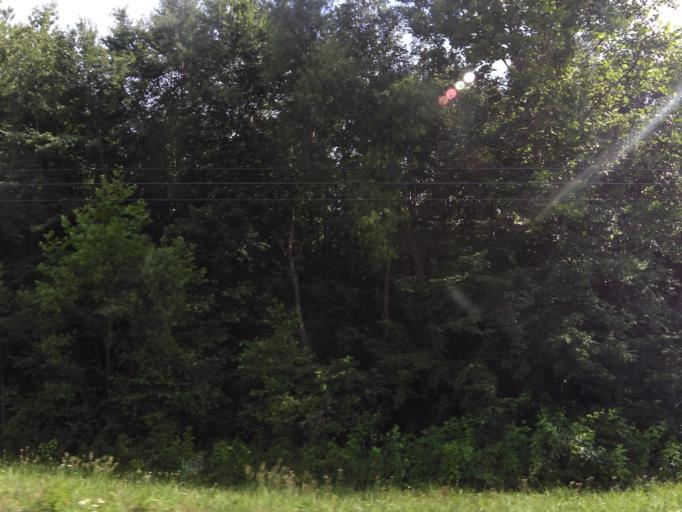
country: US
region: Tennessee
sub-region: Carroll County
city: Bruceton
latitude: 36.0362
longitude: -88.2223
